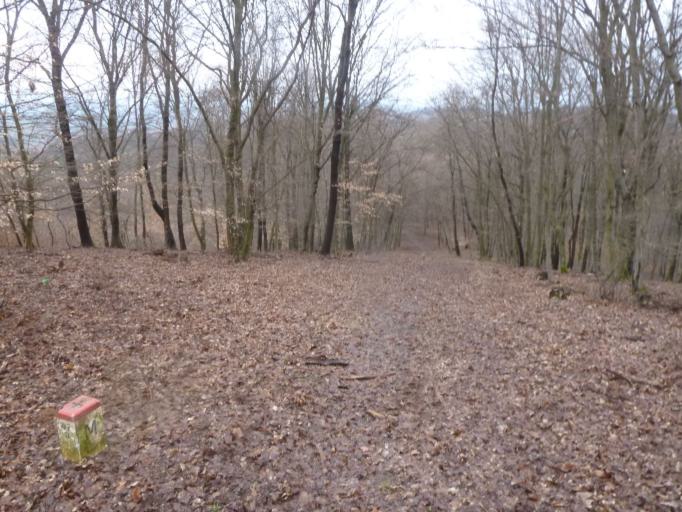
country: HU
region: Borsod-Abauj-Zemplen
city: Ozd
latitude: 48.2630
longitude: 20.2284
